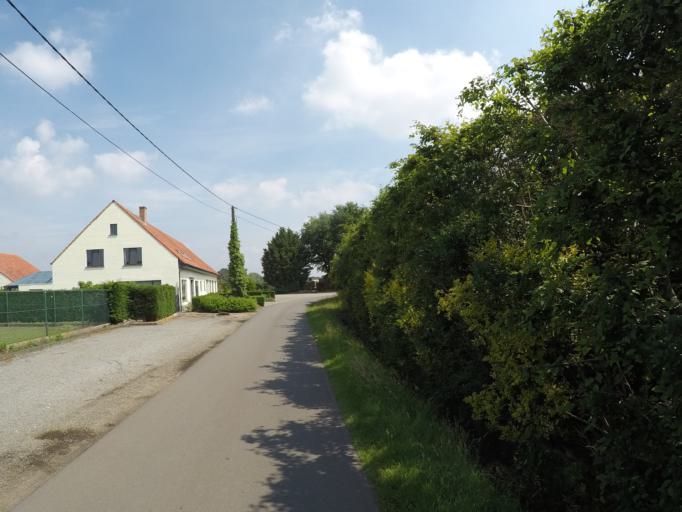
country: BE
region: Flanders
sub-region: Provincie Antwerpen
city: Brecht
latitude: 51.3572
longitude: 4.6134
